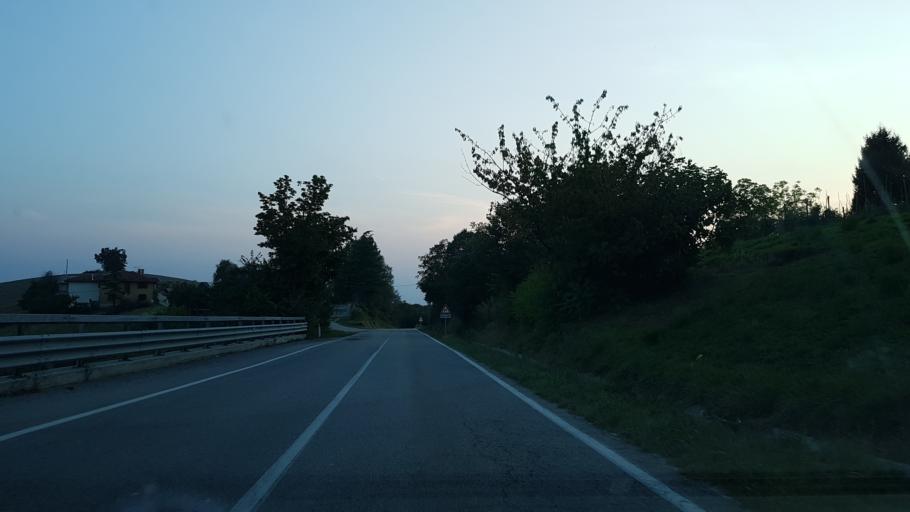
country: IT
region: Piedmont
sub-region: Provincia di Cuneo
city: Novello
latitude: 44.5851
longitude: 7.9210
